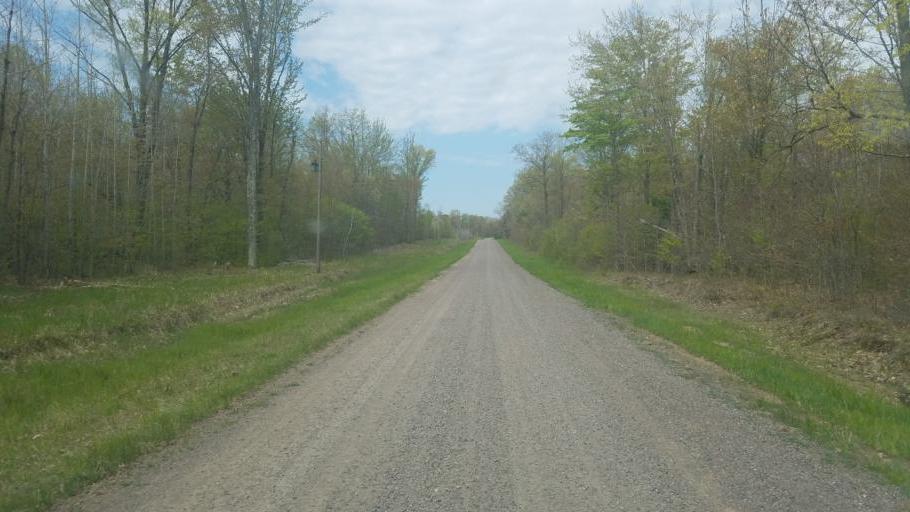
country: US
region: Wisconsin
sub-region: Clark County
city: Neillsville
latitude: 44.4514
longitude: -90.4585
